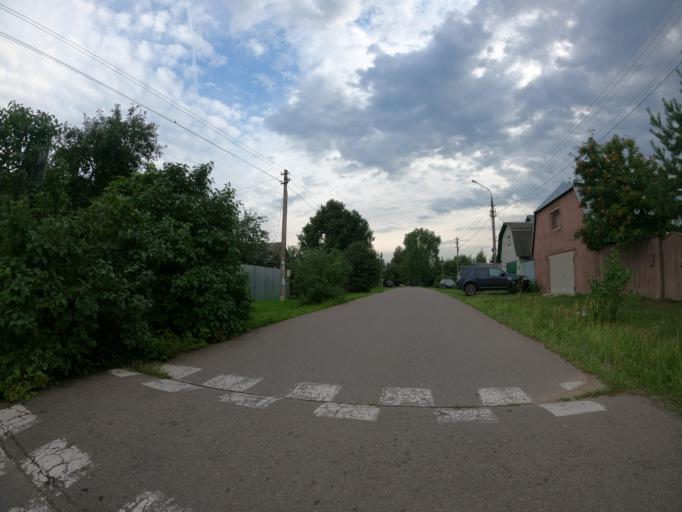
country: RU
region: Moskovskaya
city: Rodniki
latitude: 55.6834
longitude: 38.0952
